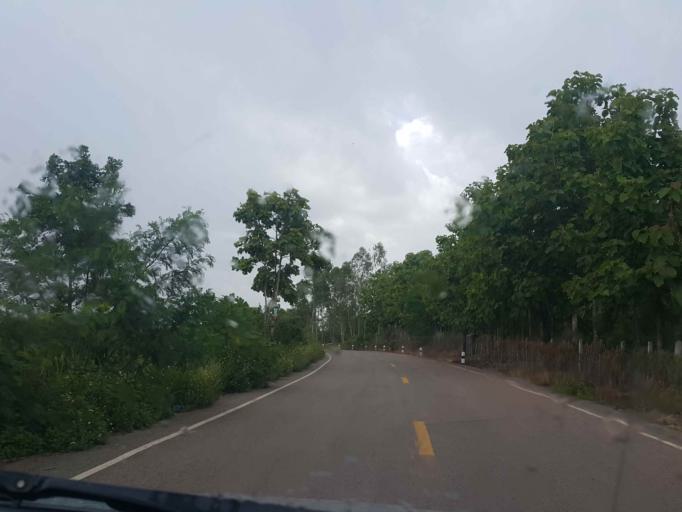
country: TH
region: Phayao
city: Dok Kham Tai
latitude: 19.0335
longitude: 99.9574
